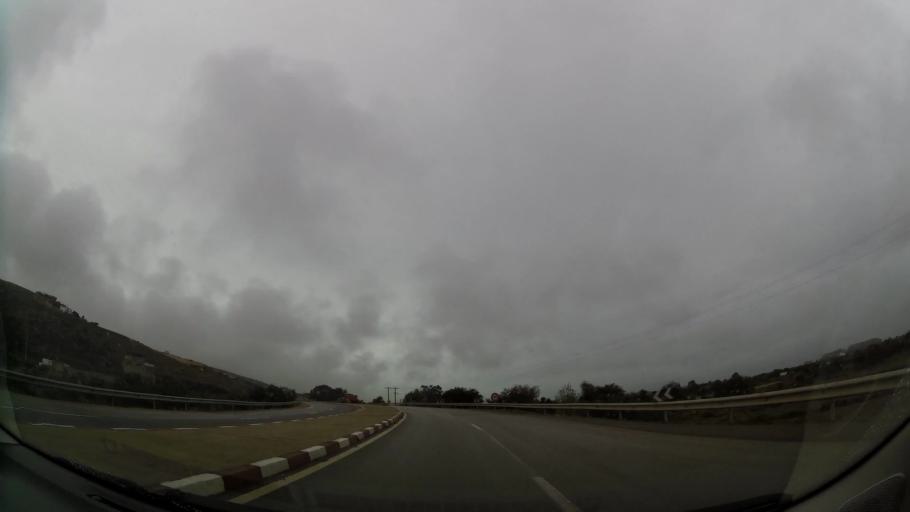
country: MA
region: Taza-Al Hoceima-Taounate
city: Imzourene
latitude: 35.1810
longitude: -3.8788
